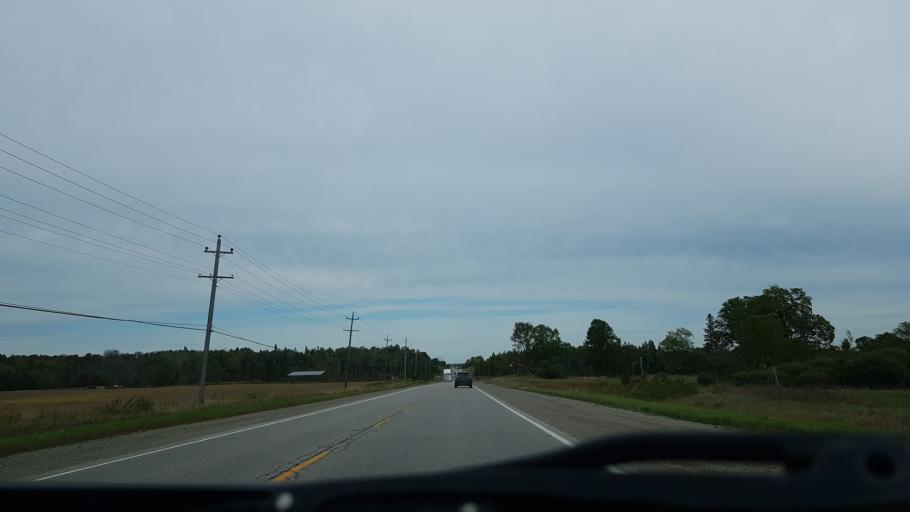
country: CA
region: Ontario
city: Orangeville
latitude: 43.7925
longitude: -80.0705
